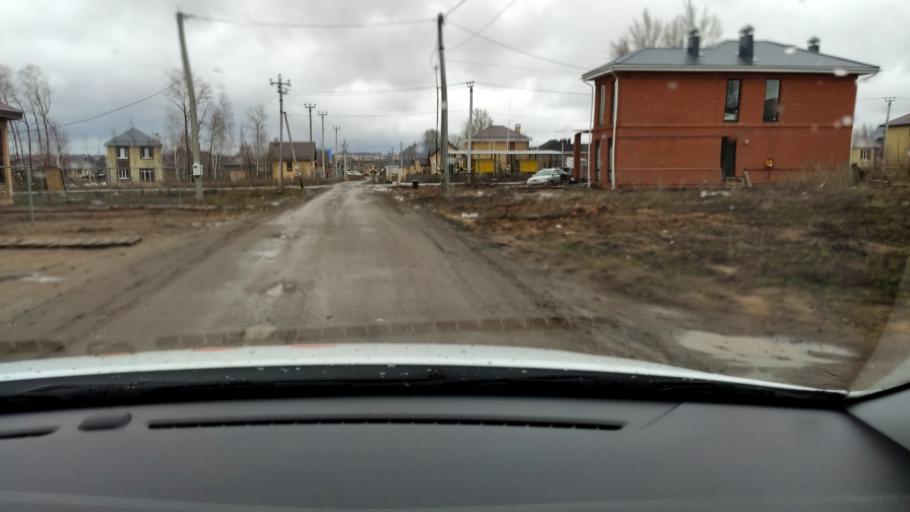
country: RU
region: Tatarstan
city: Stolbishchi
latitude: 55.7187
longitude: 49.3043
